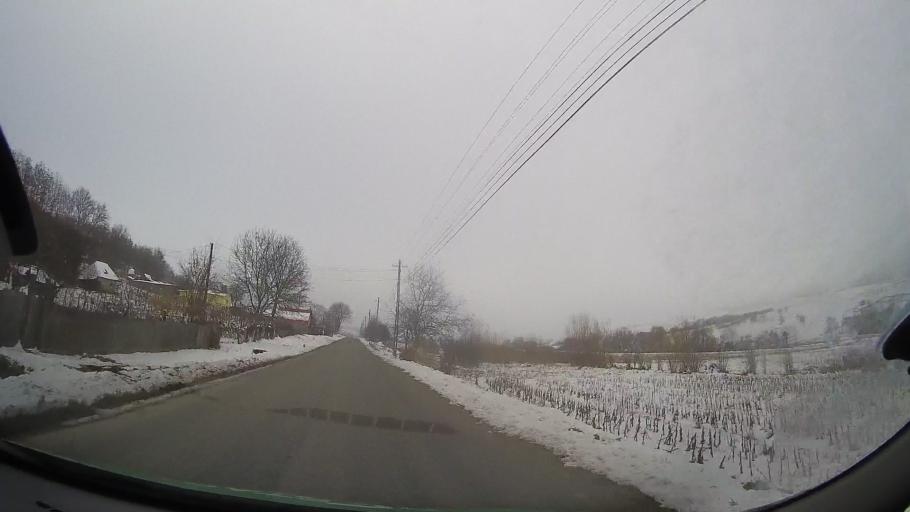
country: RO
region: Bacau
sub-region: Comuna Vultureni
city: Vultureni
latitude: 46.3228
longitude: 27.2924
